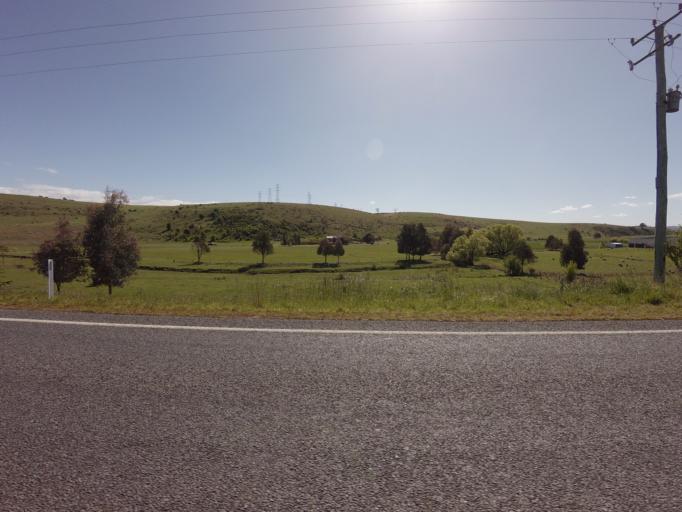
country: AU
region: Tasmania
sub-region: Derwent Valley
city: New Norfolk
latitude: -42.6618
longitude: 146.9345
